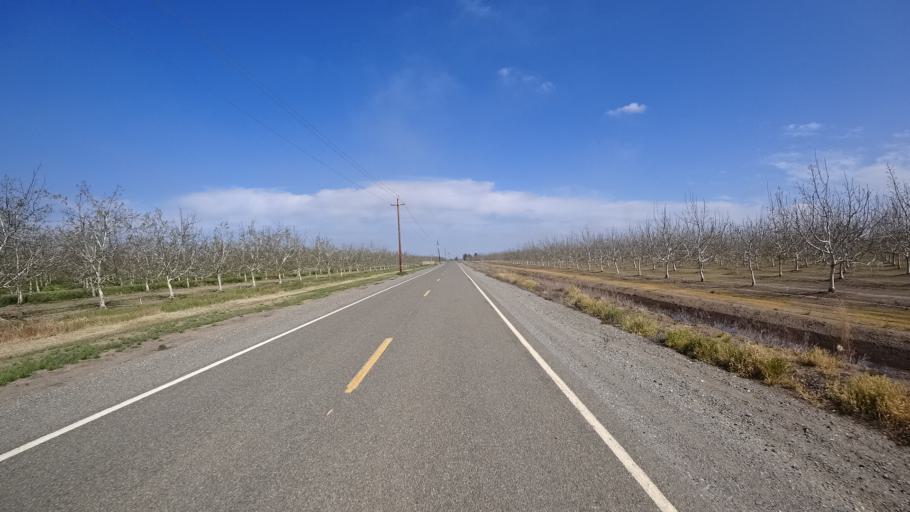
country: US
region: California
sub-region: Butte County
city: Biggs
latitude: 39.4438
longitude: -121.9301
